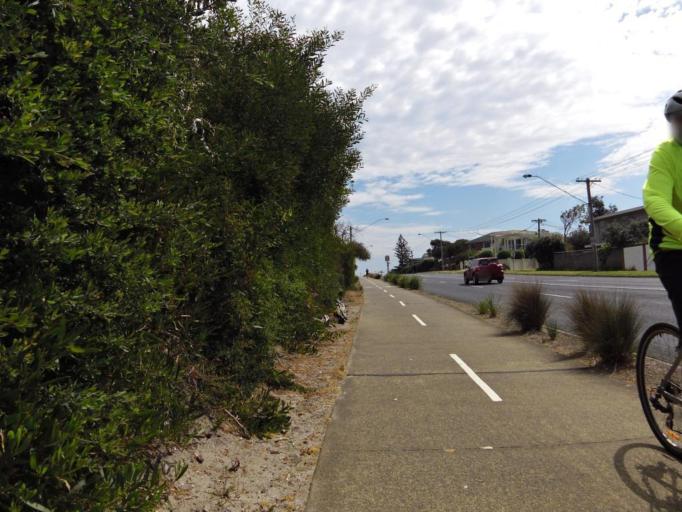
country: AU
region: Victoria
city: Beaumaris
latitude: -37.9855
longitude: 145.0248
